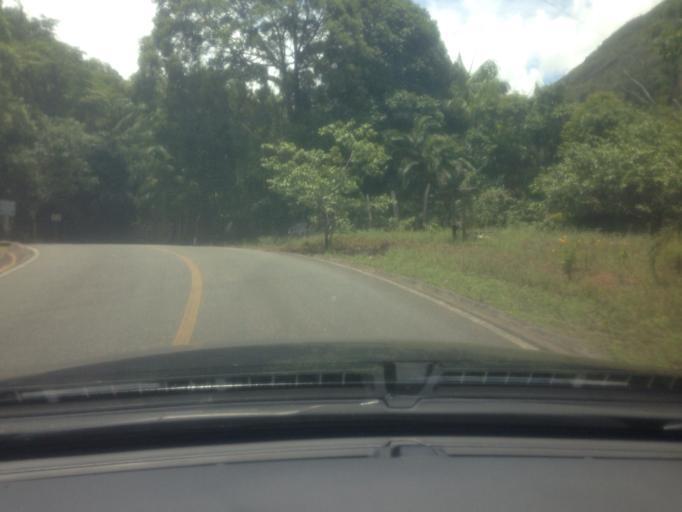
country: BR
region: Espirito Santo
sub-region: Guarapari
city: Guarapari
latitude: -20.5966
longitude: -40.5390
